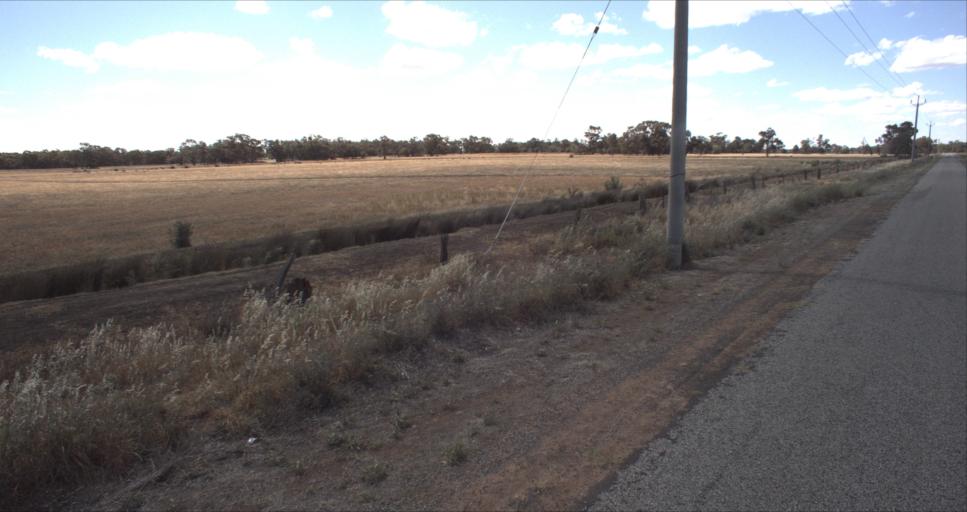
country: AU
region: New South Wales
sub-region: Leeton
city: Leeton
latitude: -34.5242
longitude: 146.2221
